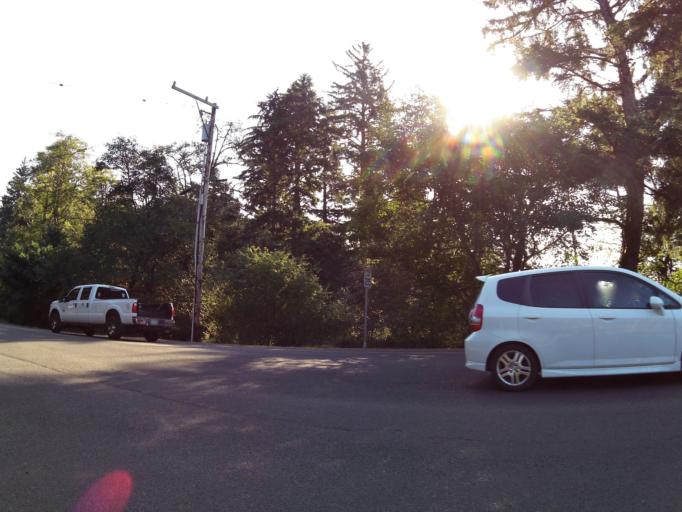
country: US
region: Oregon
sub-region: Clatsop County
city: Warrenton
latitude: 46.1828
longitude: -123.9615
